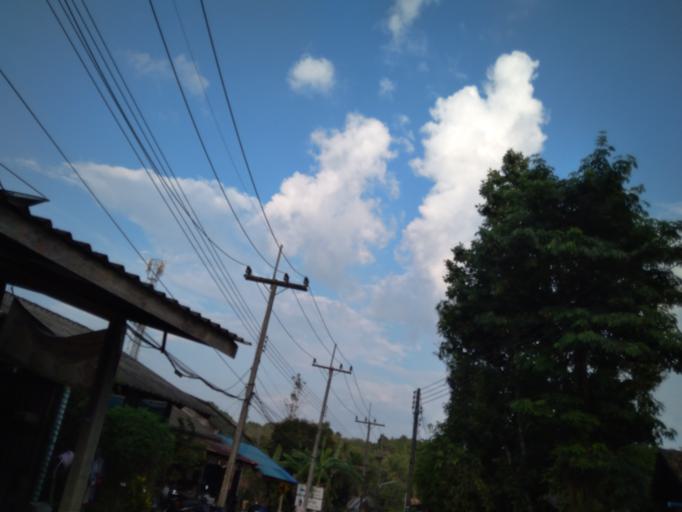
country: TH
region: Phangnga
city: Ko Yao
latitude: 8.1369
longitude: 98.6235
